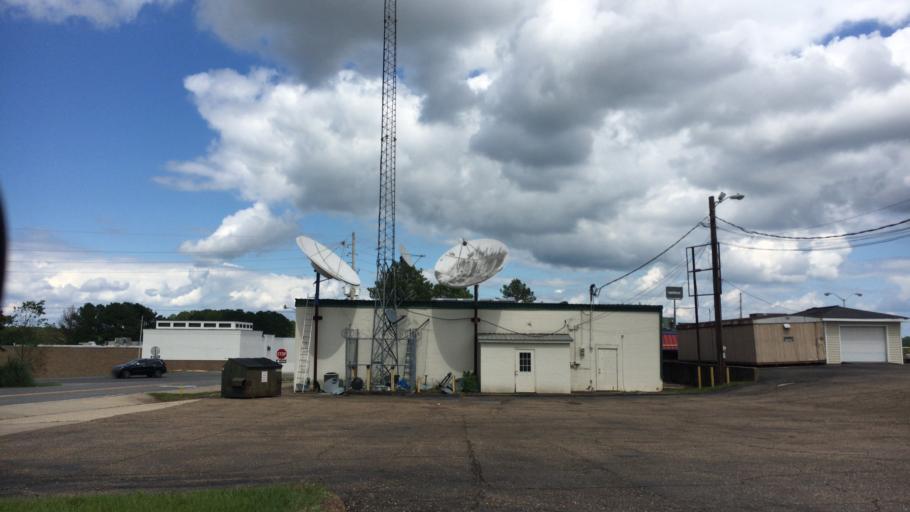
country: US
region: Louisiana
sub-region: Lincoln Parish
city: Ruston
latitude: 32.5424
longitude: -92.6394
